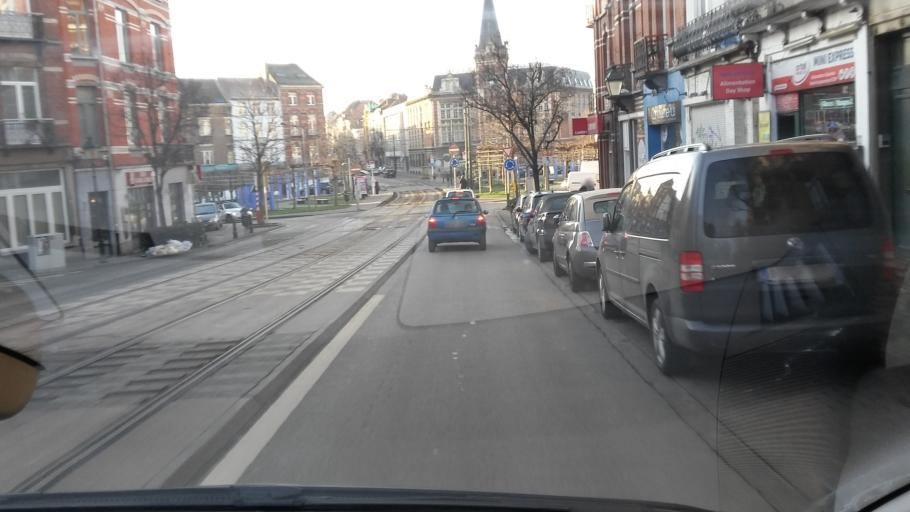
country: BE
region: Brussels Capital
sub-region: Bruxelles-Capitale
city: Brussels
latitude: 50.8377
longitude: 4.3968
